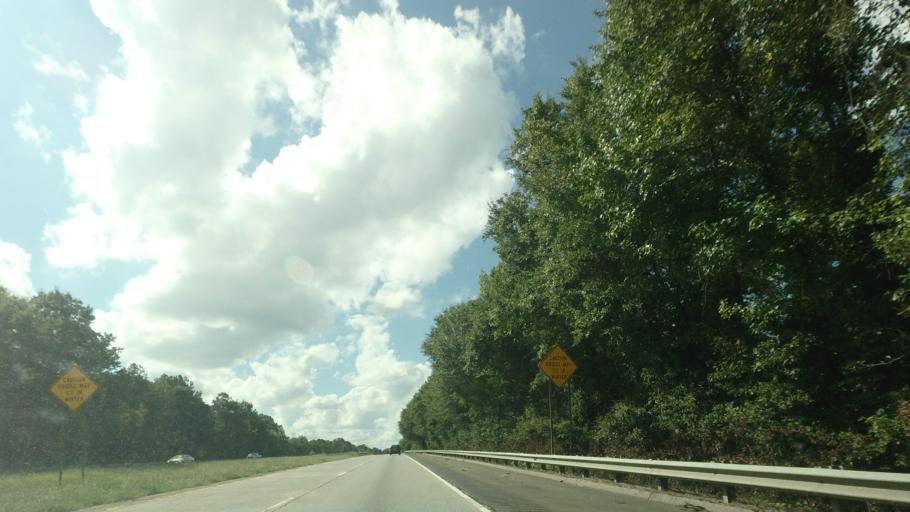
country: US
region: Georgia
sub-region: Bibb County
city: Macon
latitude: 32.8239
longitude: -83.5965
